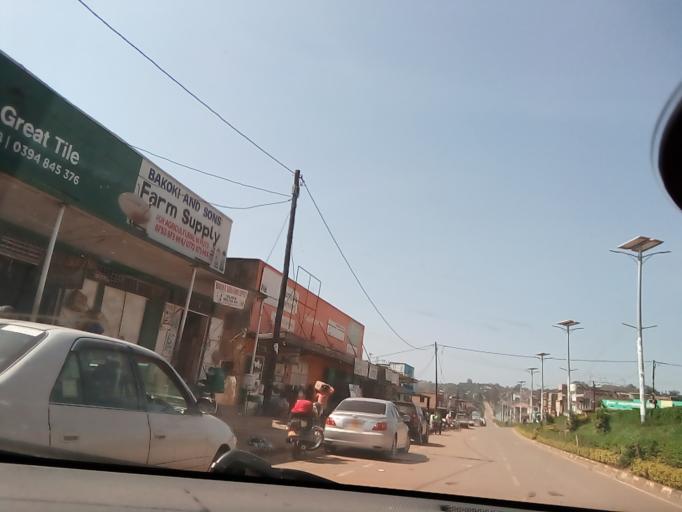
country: UG
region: Central Region
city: Masaka
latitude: -0.3427
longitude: 31.7397
